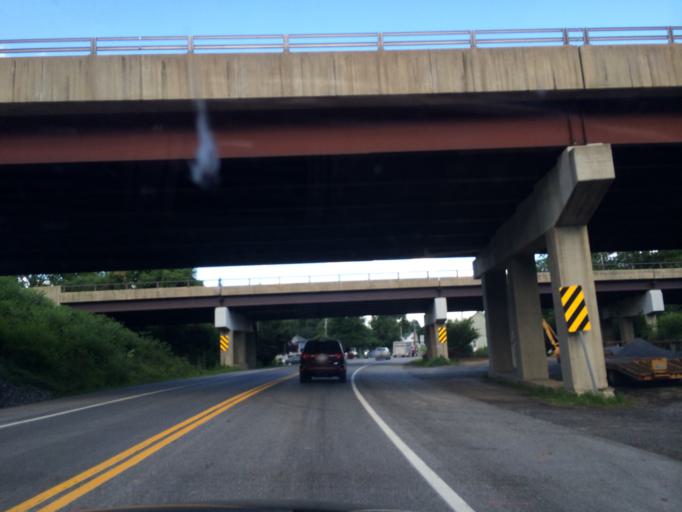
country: US
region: Maryland
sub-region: Frederick County
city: Thurmont
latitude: 39.6251
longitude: -77.4190
